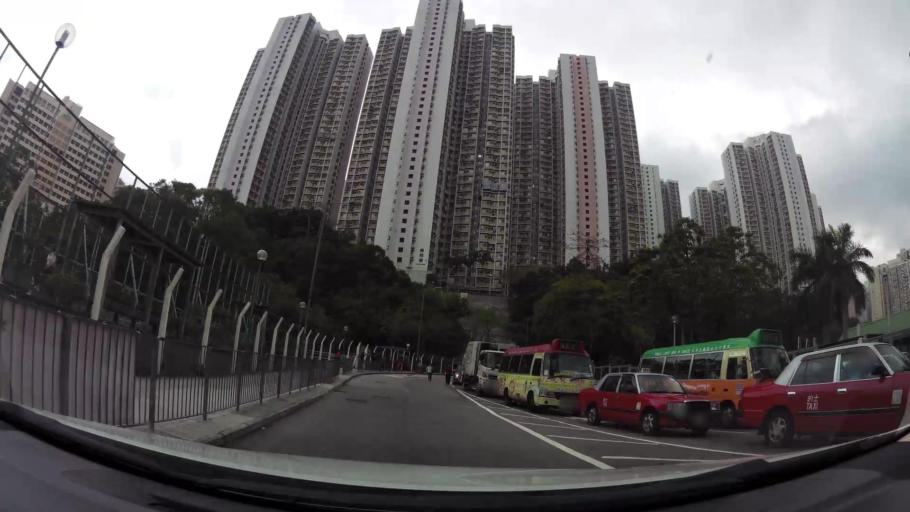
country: HK
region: Kowloon City
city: Kowloon
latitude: 22.3204
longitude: 114.2273
